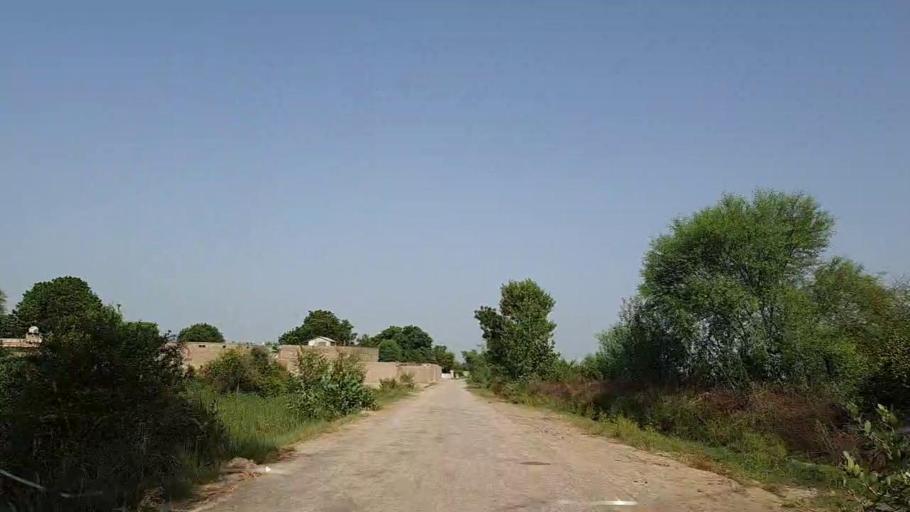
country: PK
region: Sindh
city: Kandiaro
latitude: 27.0714
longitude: 68.1574
